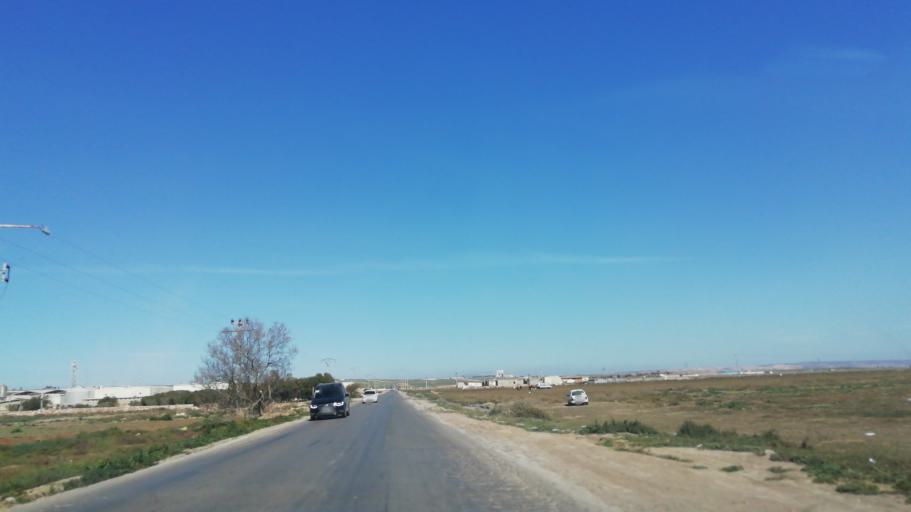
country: DZ
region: Oran
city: Es Senia
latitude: 35.5169
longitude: -0.5889
